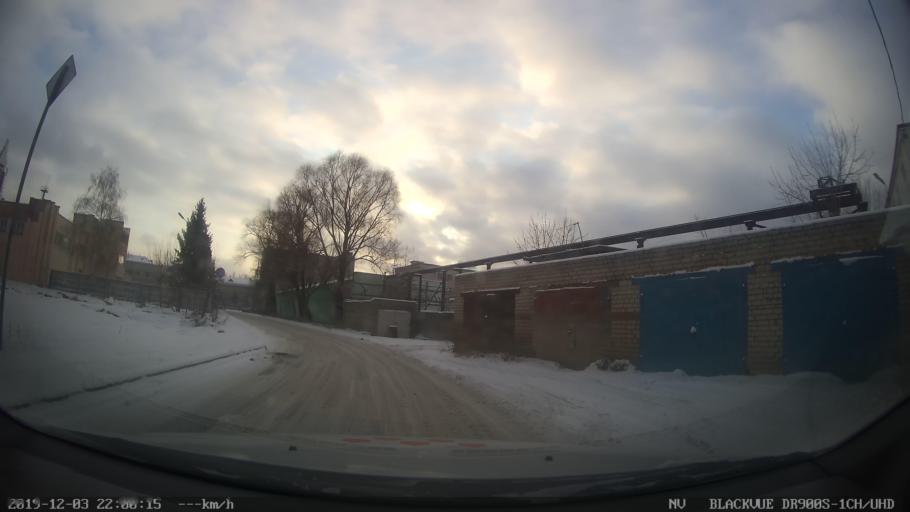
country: RU
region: Tatarstan
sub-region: Gorod Kazan'
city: Kazan
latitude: 55.7619
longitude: 49.1454
